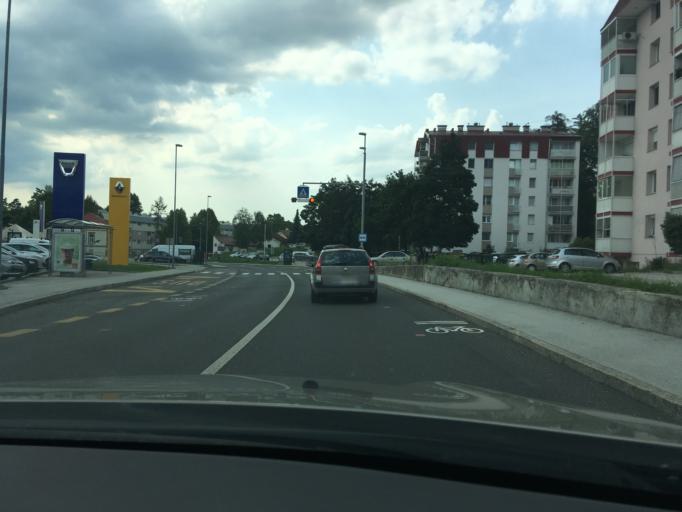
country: SI
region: Novo Mesto
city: Novo Mesto
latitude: 45.7999
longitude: 15.1756
